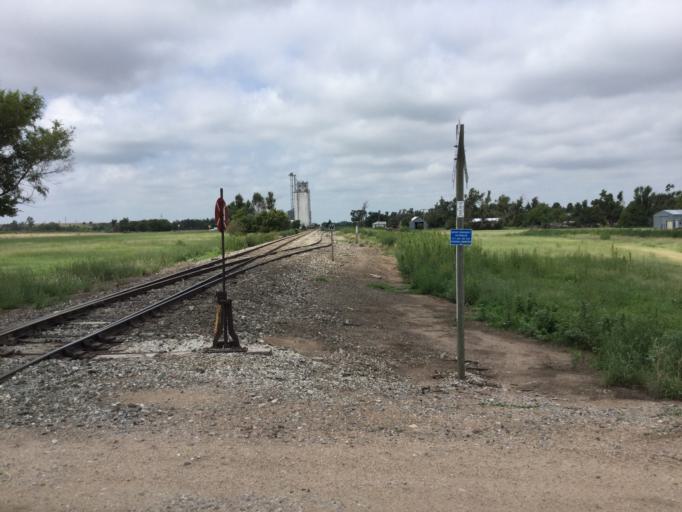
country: US
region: Kansas
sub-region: Rush County
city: La Crosse
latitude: 38.4680
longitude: -99.5485
